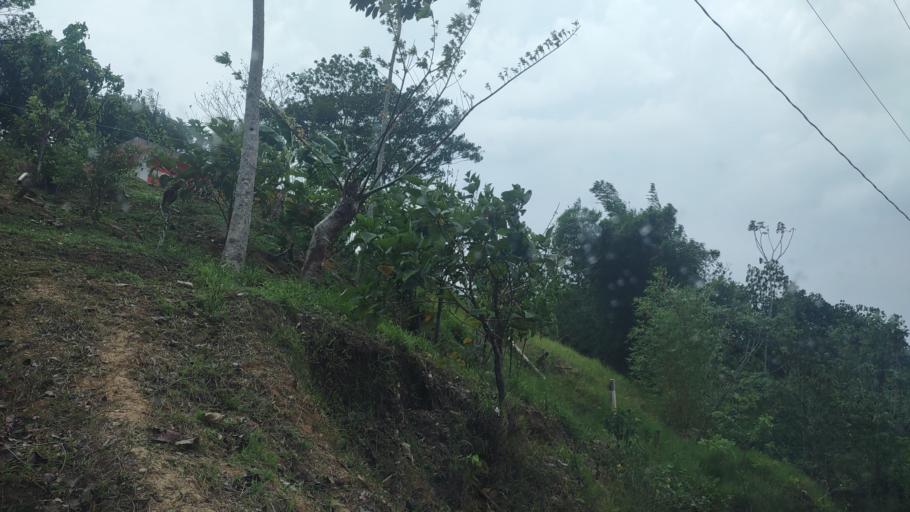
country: MX
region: Veracruz
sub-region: Uxpanapa
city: Poblado 10
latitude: 17.4524
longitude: -94.1013
